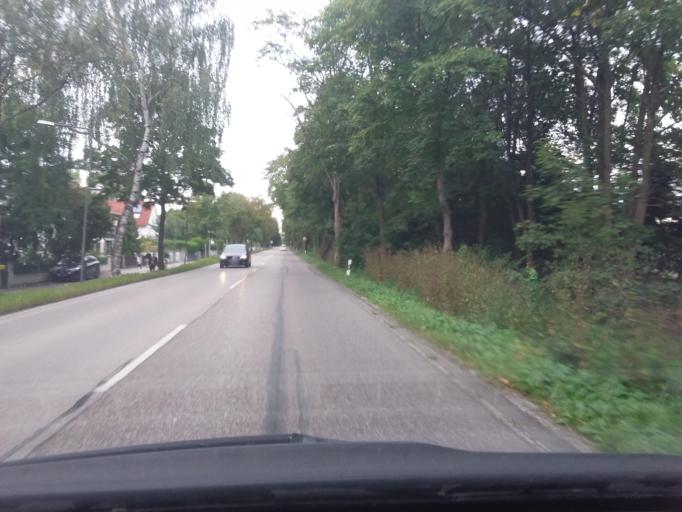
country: DE
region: Bavaria
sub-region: Upper Bavaria
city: Hebertshausen
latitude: 48.2556
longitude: 11.4779
